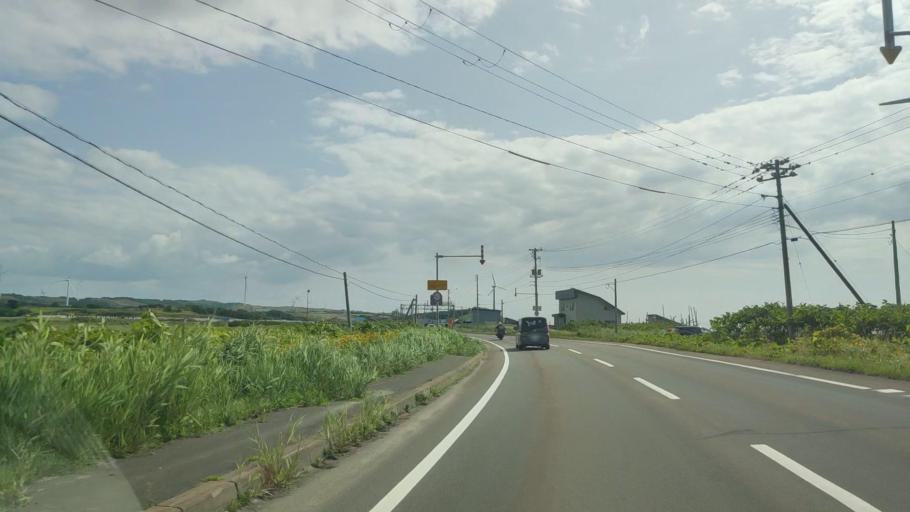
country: JP
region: Hokkaido
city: Rumoi
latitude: 44.2682
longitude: 141.6550
